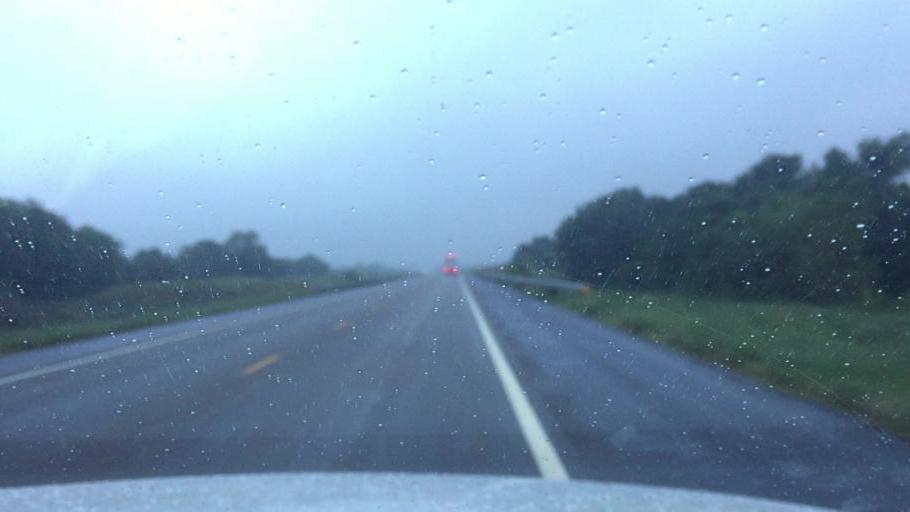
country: US
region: Kansas
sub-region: Montgomery County
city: Cherryvale
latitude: 37.4108
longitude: -95.4993
